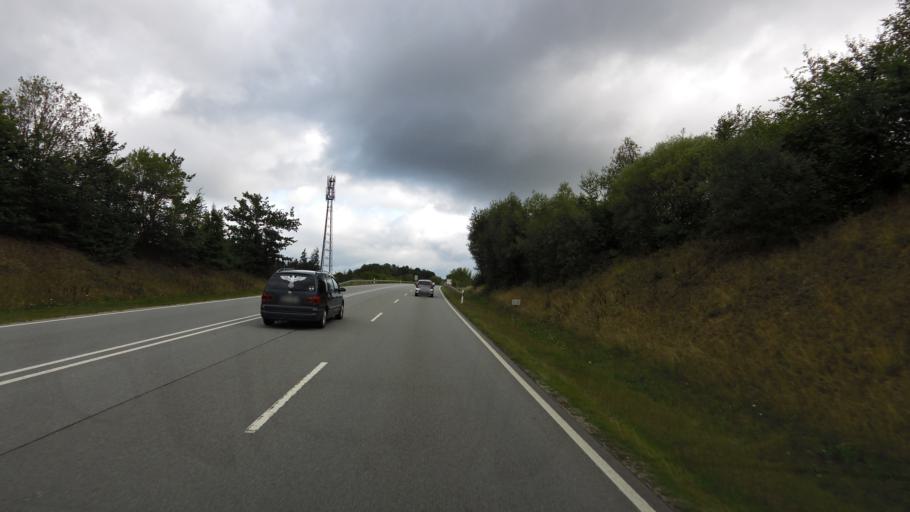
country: DE
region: Bavaria
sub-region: Upper Palatinate
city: Traitsching
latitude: 49.1596
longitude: 12.6550
